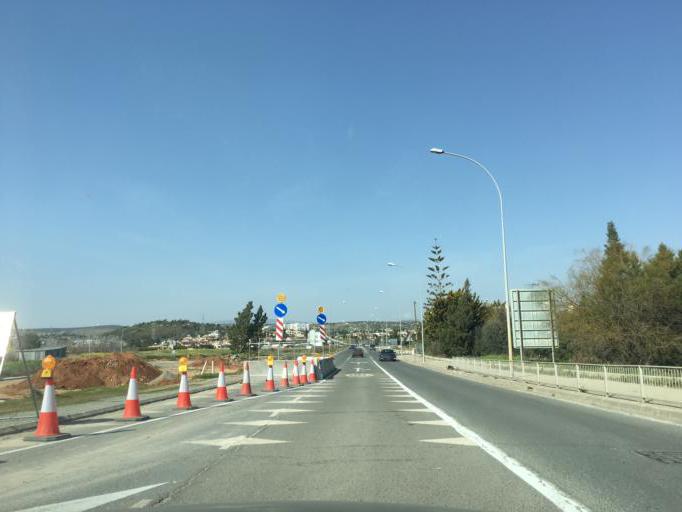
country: CY
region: Limassol
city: Pano Polemidia
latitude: 34.6901
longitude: 32.9892
